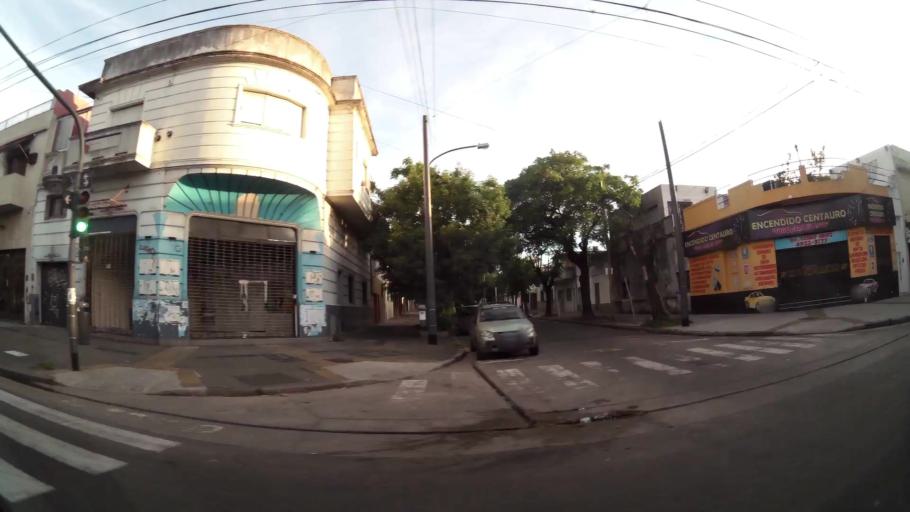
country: AR
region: Buenos Aires F.D.
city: Villa Lugano
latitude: -34.6413
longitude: -58.4299
